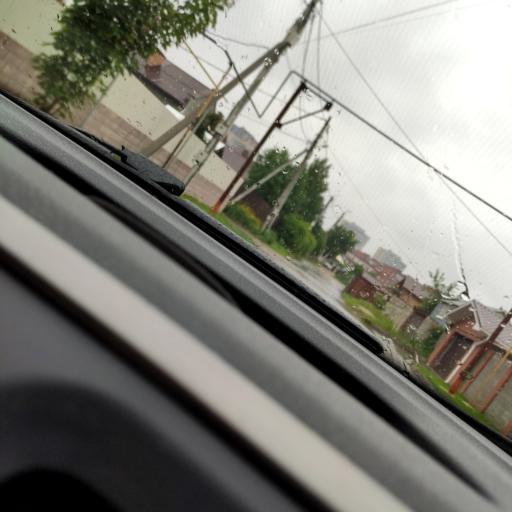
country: RU
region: Samara
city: Tol'yatti
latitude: 53.5083
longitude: 49.2435
